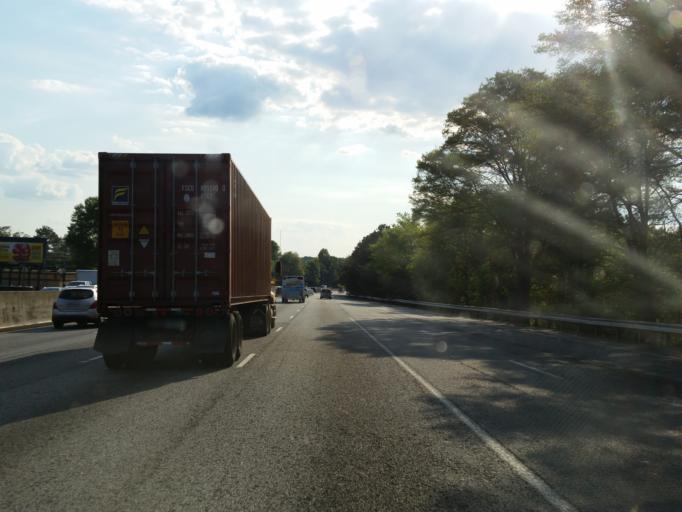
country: US
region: Georgia
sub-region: Fulton County
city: Atlanta
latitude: 33.7515
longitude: -84.4497
